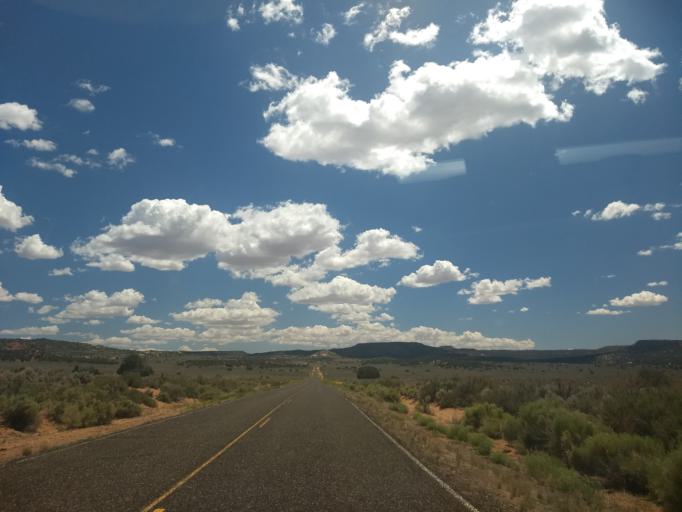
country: US
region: Utah
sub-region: Kane County
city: Kanab
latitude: 37.1669
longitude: -112.6640
